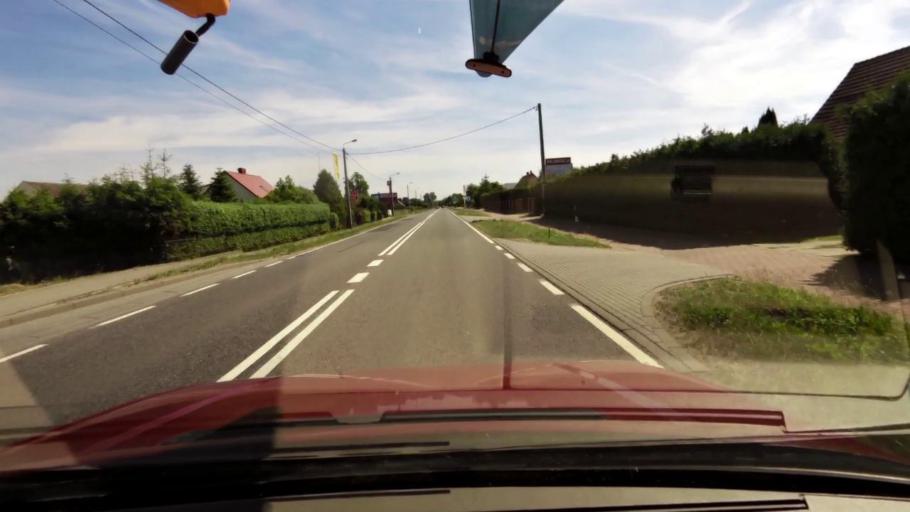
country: PL
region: Pomeranian Voivodeship
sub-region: Powiat slupski
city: Kobylnica
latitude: 54.4183
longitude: 17.0075
